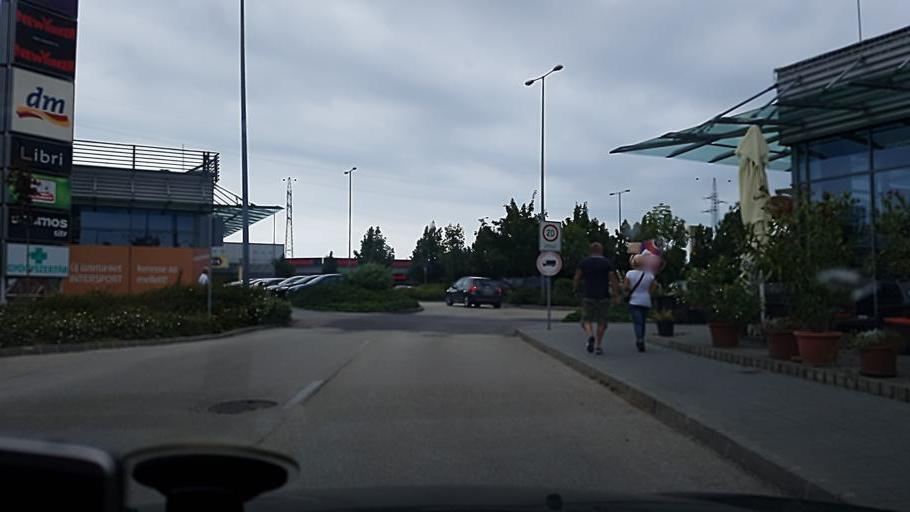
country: HU
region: Veszprem
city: Veszprem
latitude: 47.0852
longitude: 17.9260
